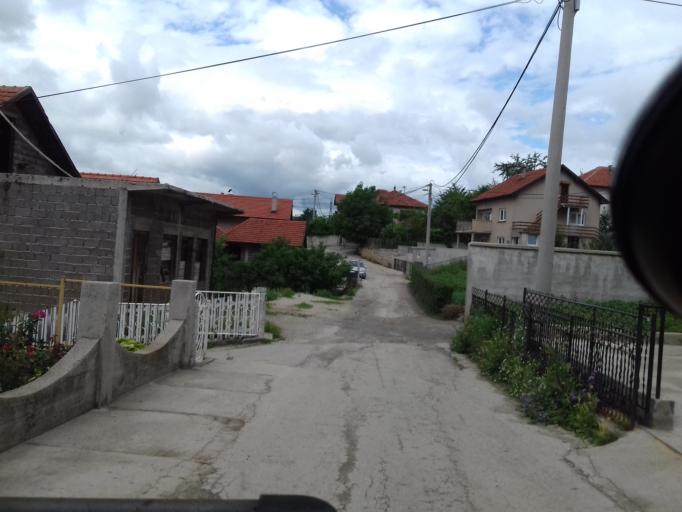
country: BA
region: Federation of Bosnia and Herzegovina
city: Zenica
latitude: 44.1976
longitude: 17.9328
